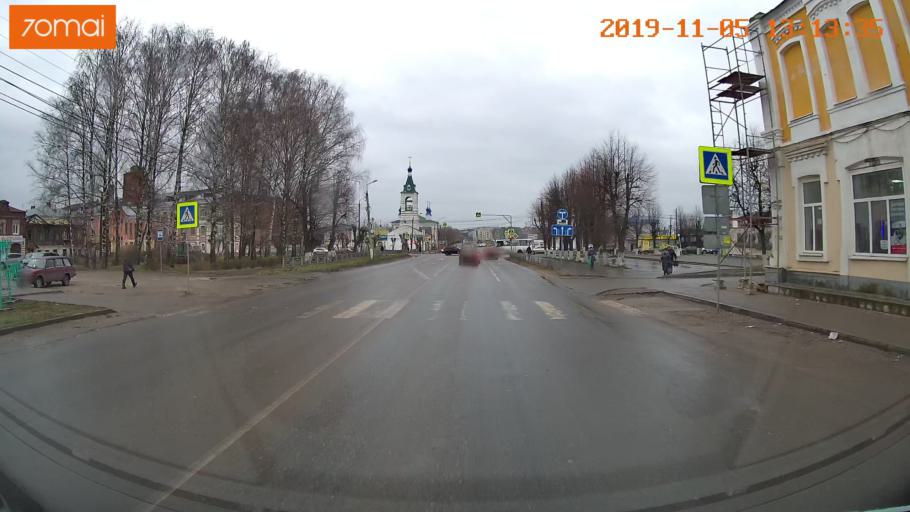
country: RU
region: Ivanovo
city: Shuya
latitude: 56.8512
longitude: 41.3560
